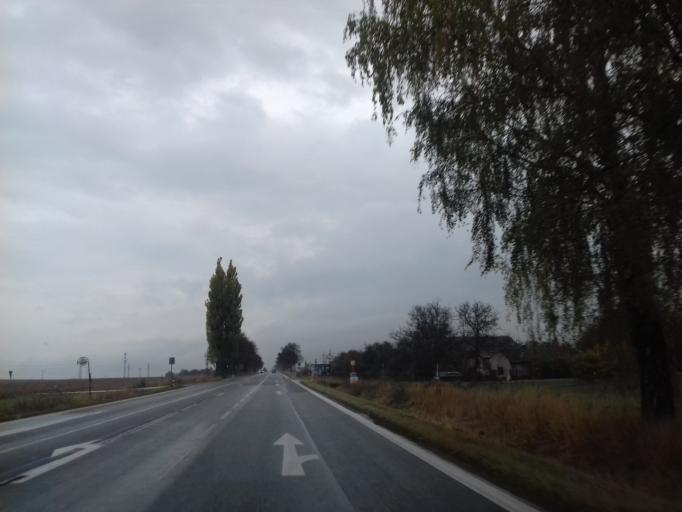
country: CZ
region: Kralovehradecky
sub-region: Okres Hradec Kralove
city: Vsestary
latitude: 50.2448
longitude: 15.7740
